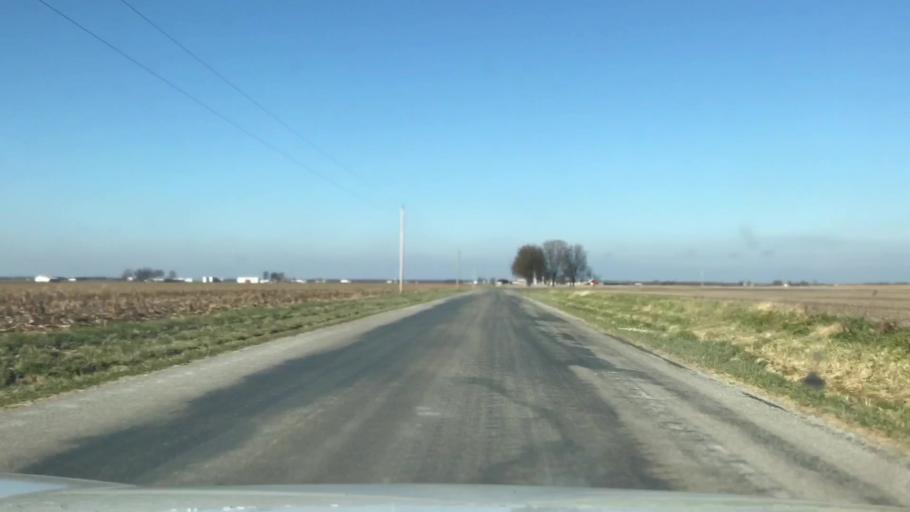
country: US
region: Illinois
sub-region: Washington County
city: Okawville
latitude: 38.4095
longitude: -89.4866
